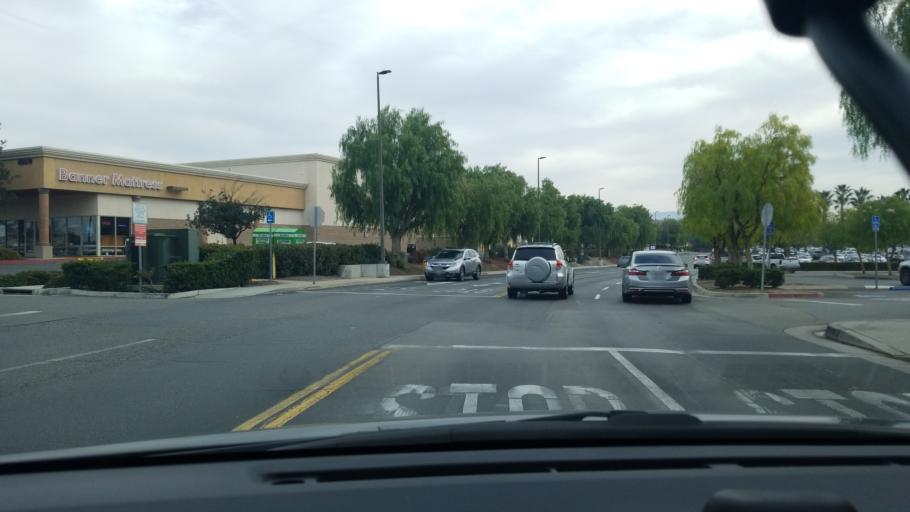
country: US
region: California
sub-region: Riverside County
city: Murrieta Hot Springs
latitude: 33.5279
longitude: -117.1529
